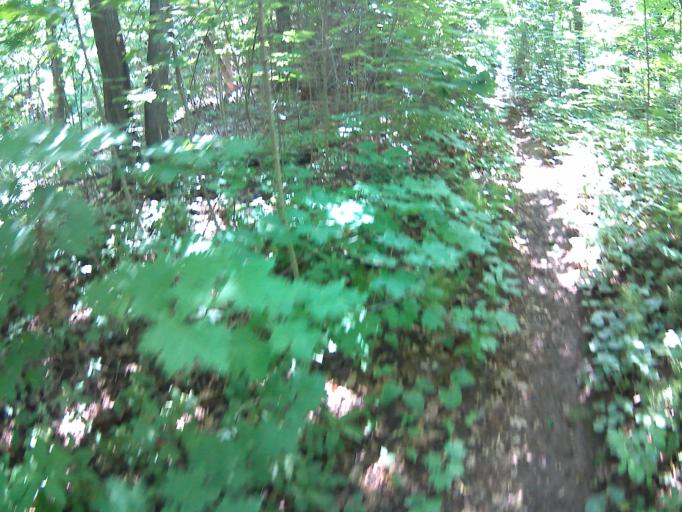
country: RU
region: Nizjnij Novgorod
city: Nizhniy Novgorod
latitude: 56.2285
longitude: 43.9238
